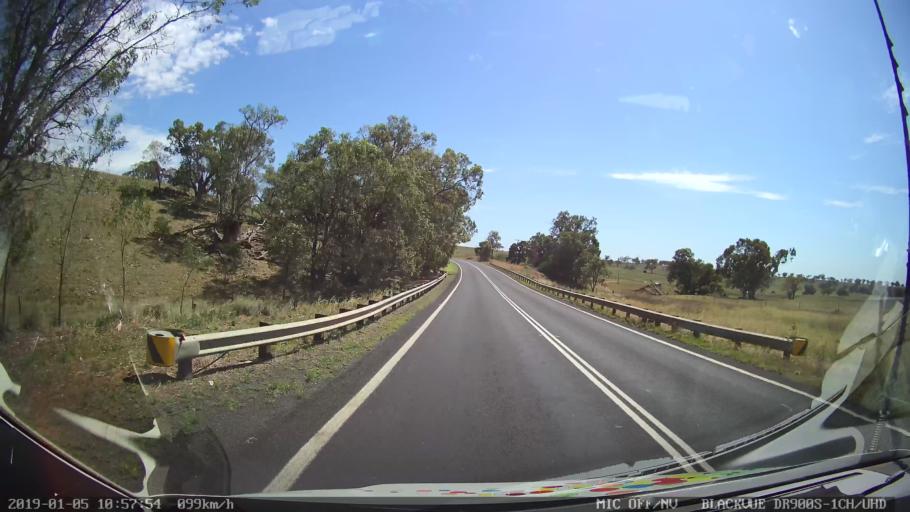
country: AU
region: New South Wales
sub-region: Warrumbungle Shire
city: Coonabarabran
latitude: -31.4271
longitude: 149.1756
